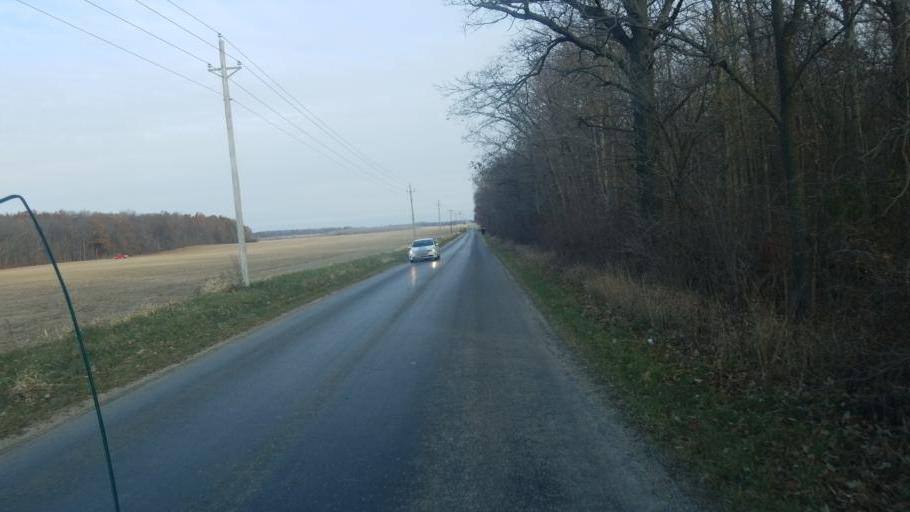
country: US
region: Indiana
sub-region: Adams County
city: Geneva
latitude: 40.5514
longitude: -84.9917
